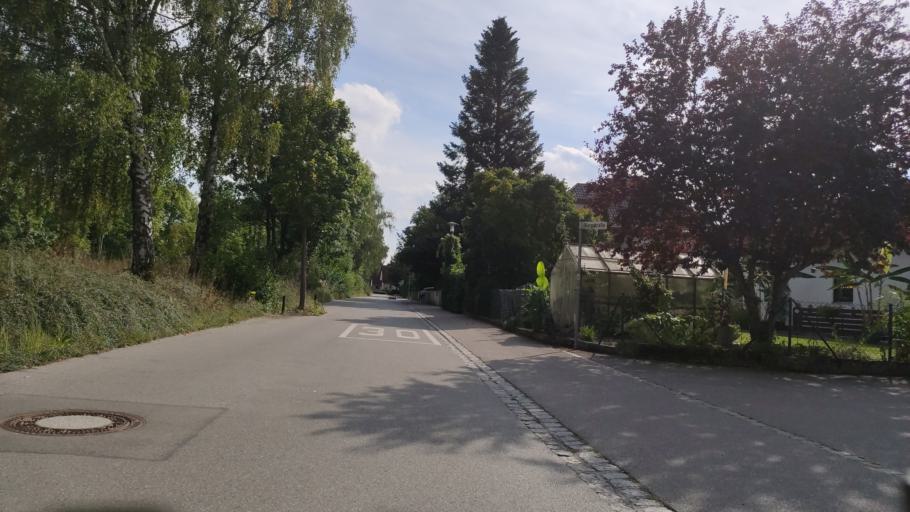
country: DE
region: Bavaria
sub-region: Swabia
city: Klosterlechfeld
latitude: 48.1542
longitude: 10.8320
